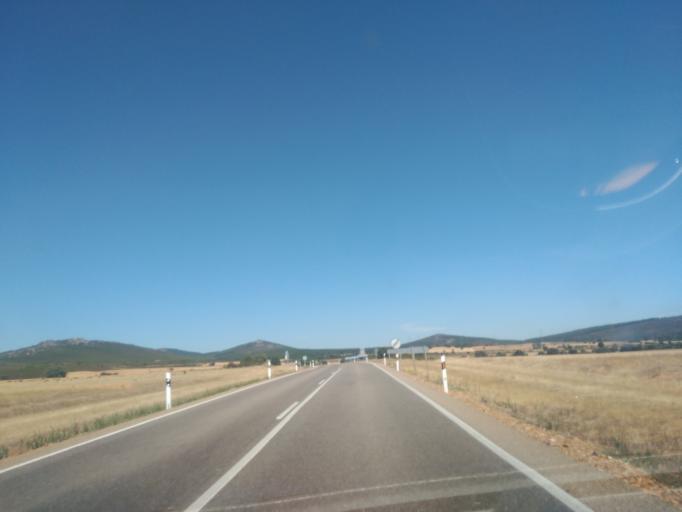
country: ES
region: Castille and Leon
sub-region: Provincia de Zamora
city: Tabara
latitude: 41.8473
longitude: -5.9821
